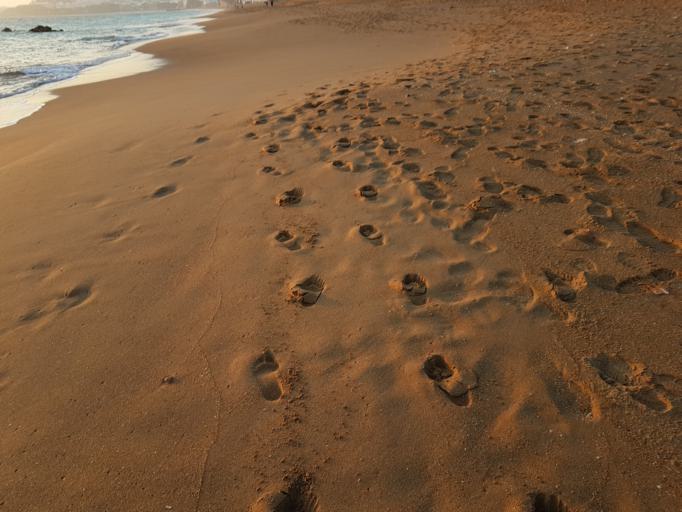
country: PT
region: Faro
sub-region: Albufeira
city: Albufeira
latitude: 37.0832
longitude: -8.2348
